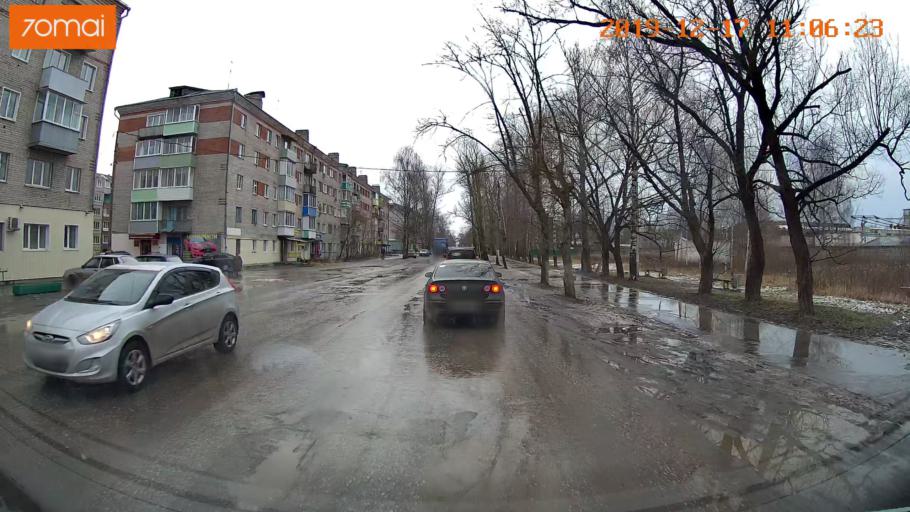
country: RU
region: Vladimir
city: Gus'-Khrustal'nyy
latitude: 55.6158
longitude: 40.6446
